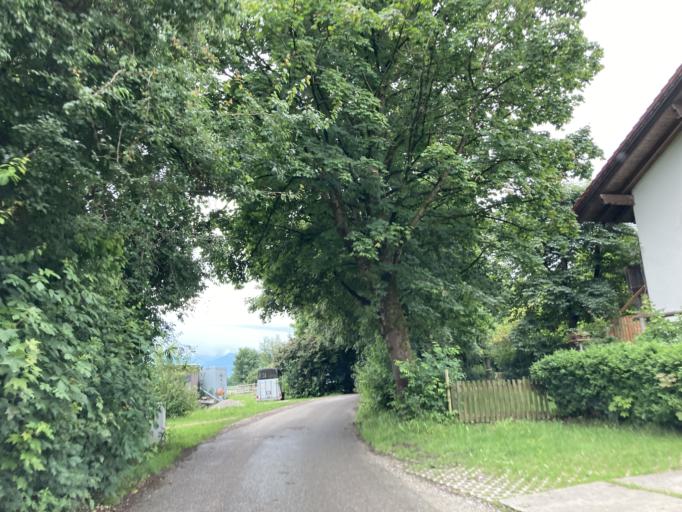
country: DE
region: Bavaria
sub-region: Upper Bavaria
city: Stephanskirchen
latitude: 47.8690
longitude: 12.1578
